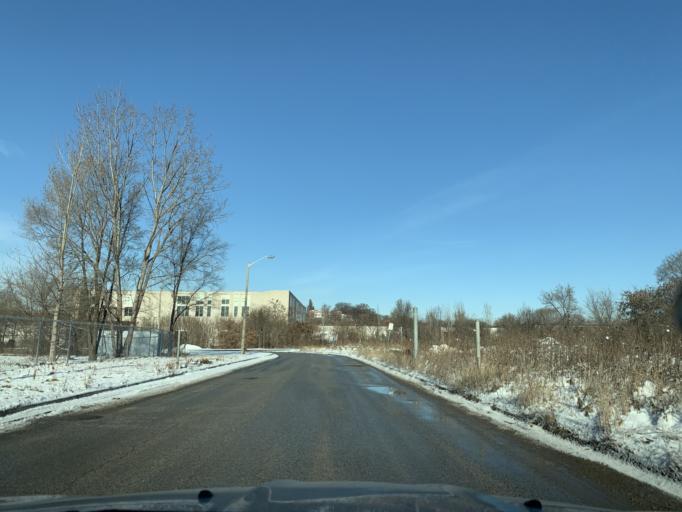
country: CA
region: Ontario
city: Toronto
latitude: 43.6747
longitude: -79.4866
